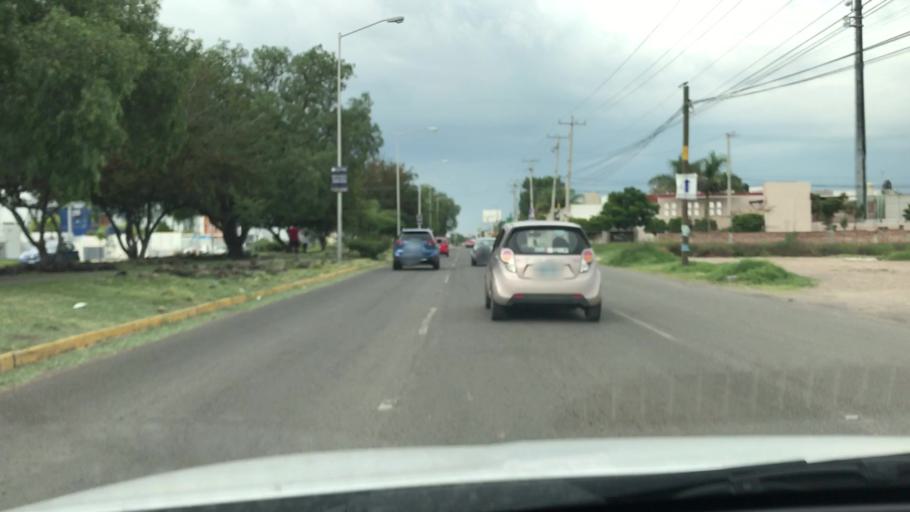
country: MX
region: Guanajuato
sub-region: Celaya
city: La Trinidad
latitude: 20.5364
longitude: -100.7895
